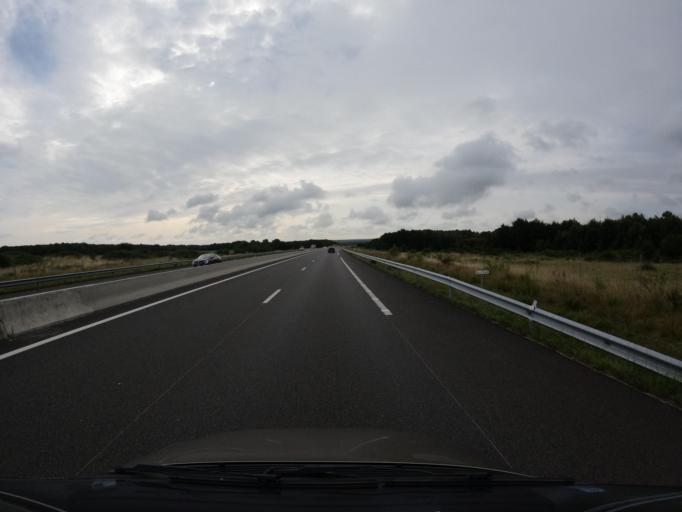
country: FR
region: Centre
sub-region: Departement d'Indre-et-Loire
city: Langeais
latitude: 47.3424
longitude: 0.4199
